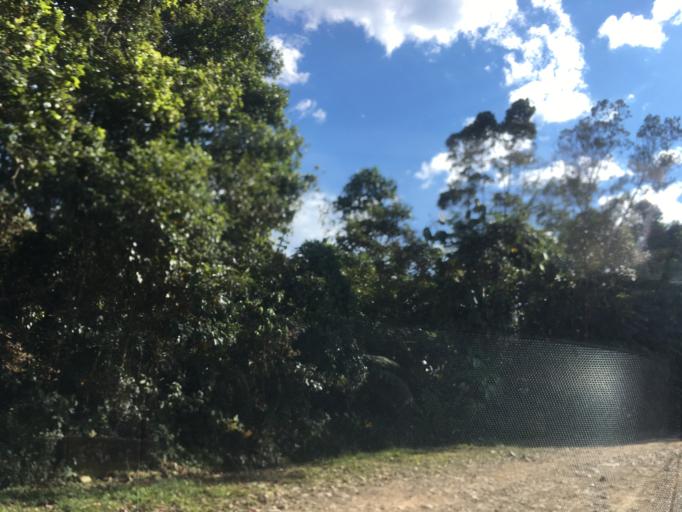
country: CO
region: Santander
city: Oiba
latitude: 6.1400
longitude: -73.1918
